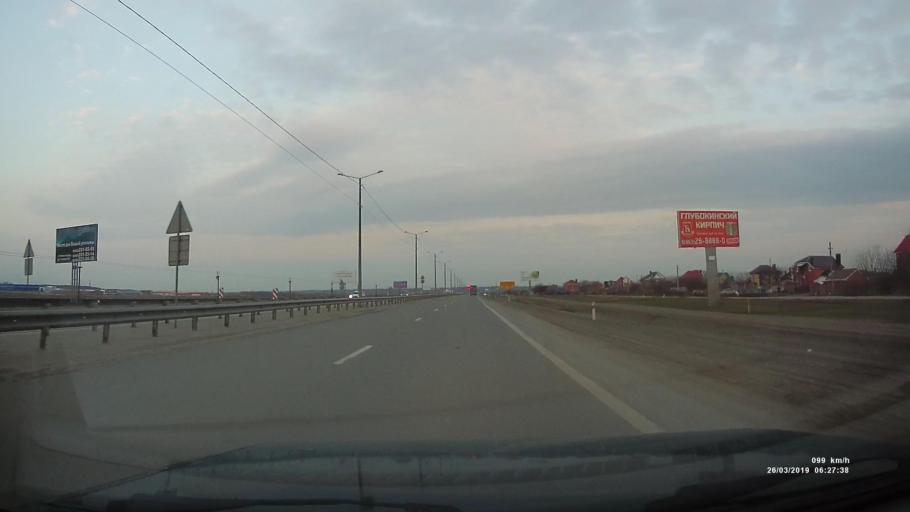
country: RU
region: Rostov
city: Kalinin
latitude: 47.2613
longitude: 39.6080
